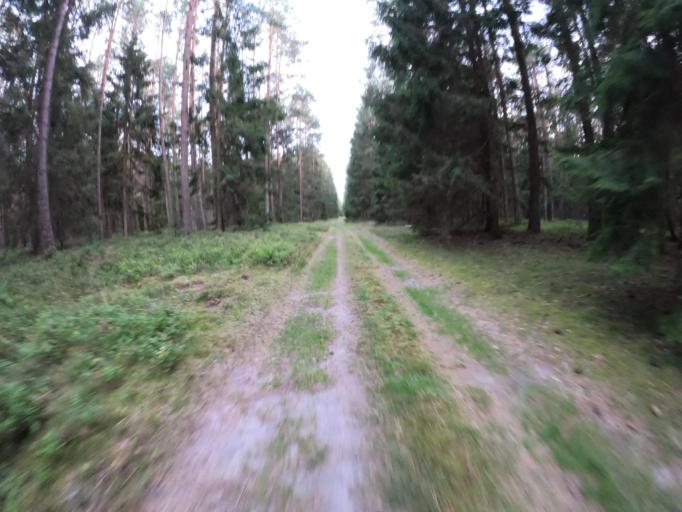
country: PL
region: West Pomeranian Voivodeship
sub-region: Powiat koszalinski
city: Sianow
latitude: 54.0920
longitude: 16.4087
